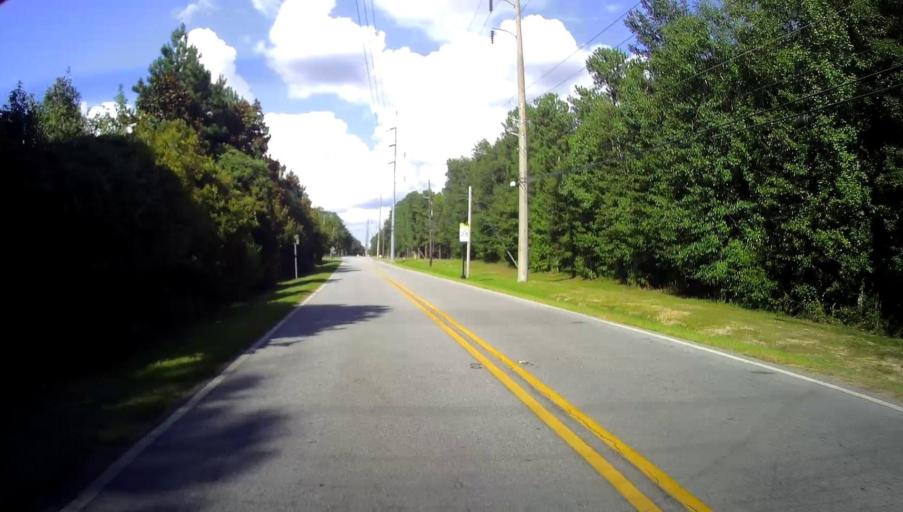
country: US
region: Georgia
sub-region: Muscogee County
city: Columbus
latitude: 32.5537
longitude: -84.8698
